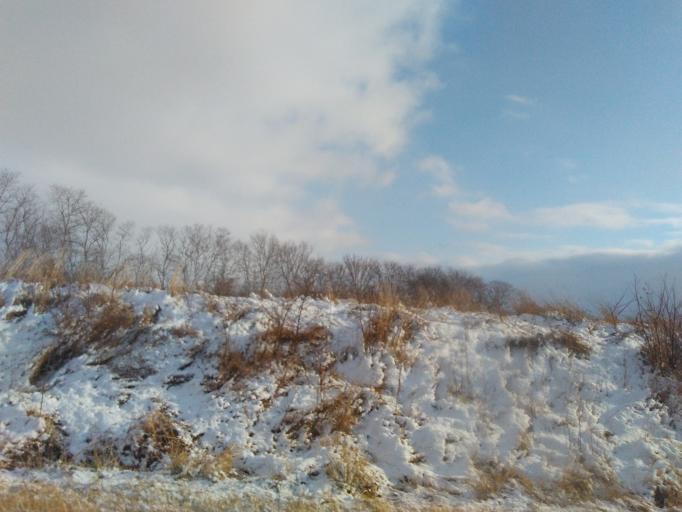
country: US
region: Illinois
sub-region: Madison County
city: Highland
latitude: 38.7658
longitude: -89.6542
